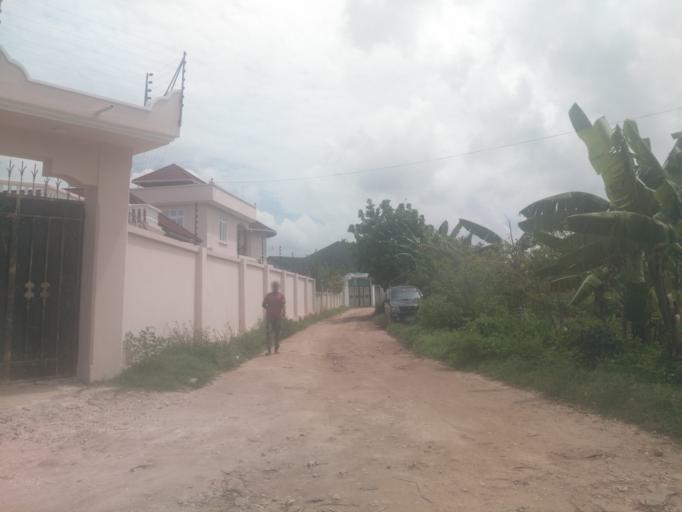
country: TZ
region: Zanzibar Urban/West
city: Zanzibar
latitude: -6.2367
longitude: 39.2136
